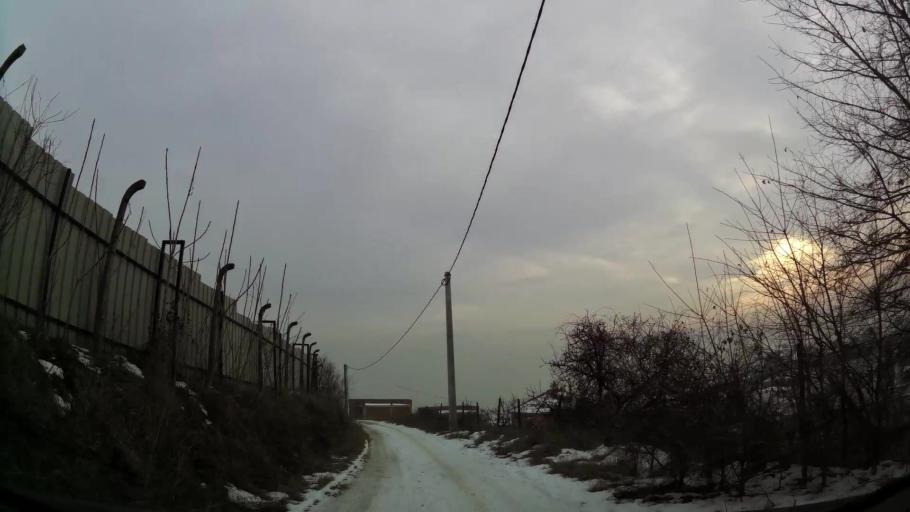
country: MK
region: Suto Orizari
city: Suto Orizare
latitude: 42.0389
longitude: 21.4310
